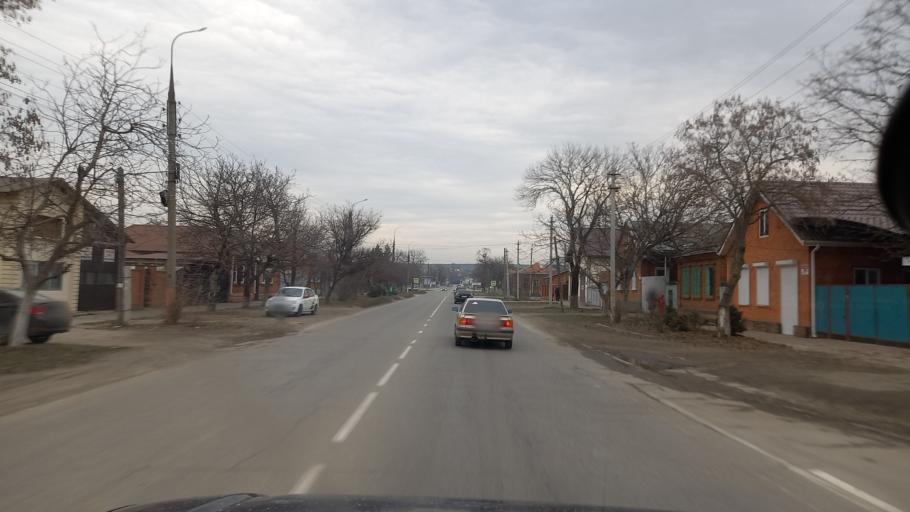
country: RU
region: Adygeya
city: Maykop
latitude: 44.5985
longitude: 40.1291
